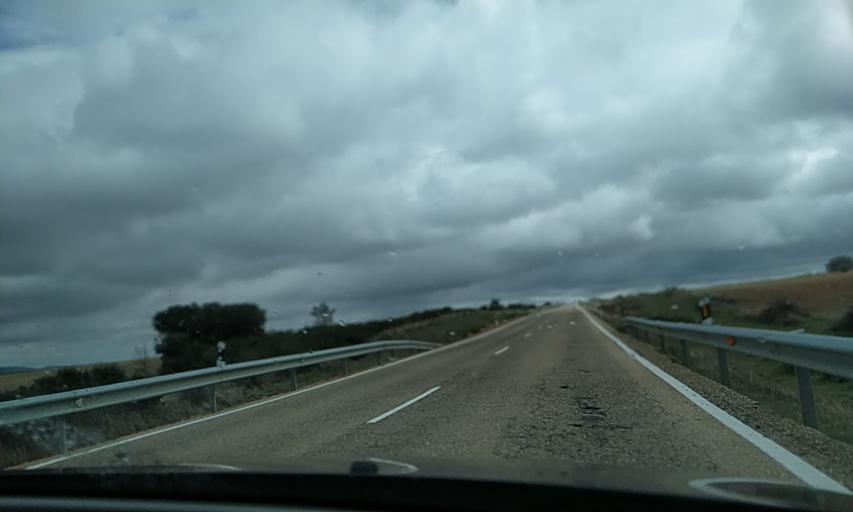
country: ES
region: Castille and Leon
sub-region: Provincia de Zamora
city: Tabara
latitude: 41.8518
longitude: -5.9884
